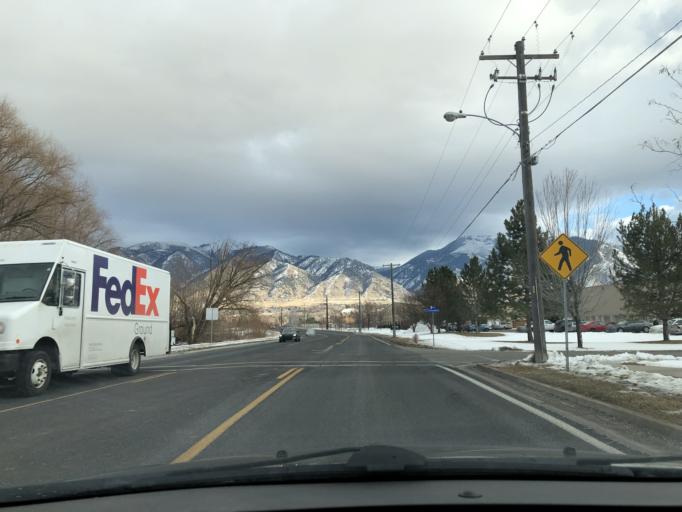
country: US
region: Utah
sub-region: Cache County
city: Providence
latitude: 41.7028
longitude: -111.8466
